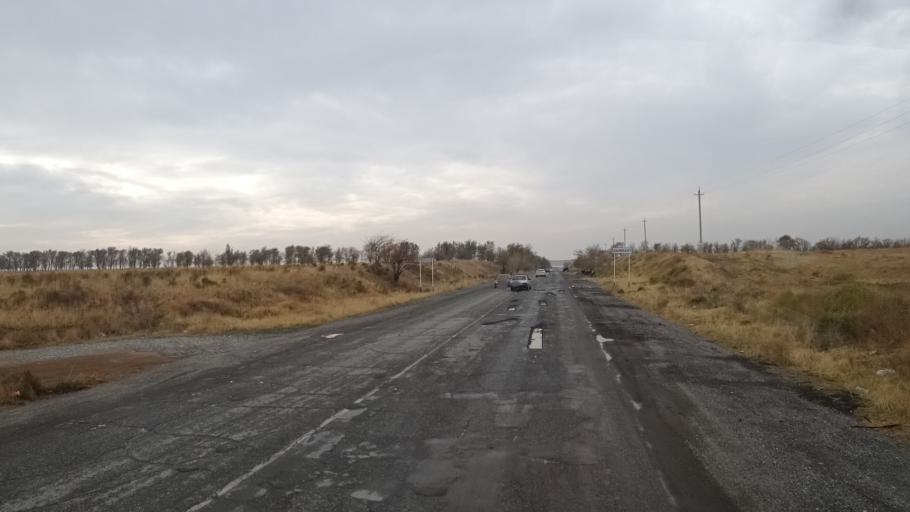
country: KZ
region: Ongtustik Qazaqstan
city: Aksu
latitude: 42.4320
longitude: 69.7125
